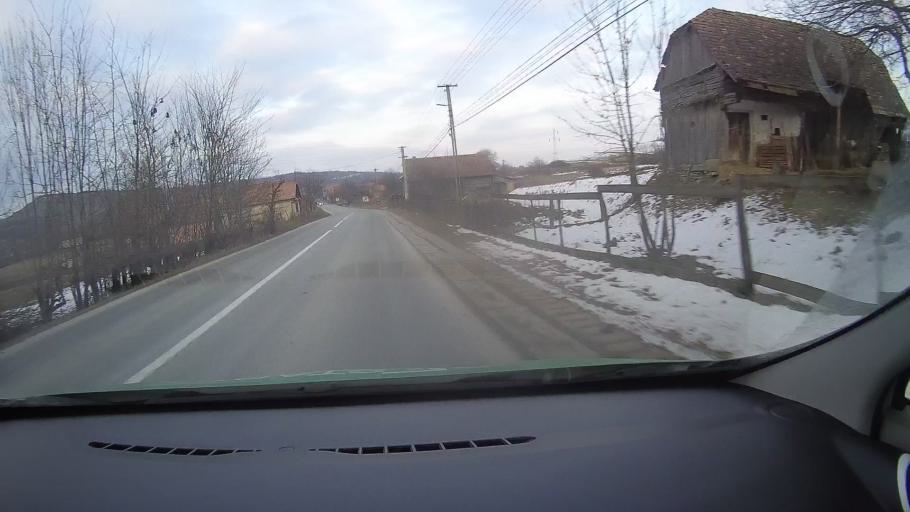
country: RO
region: Harghita
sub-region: Comuna Simonesti
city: Simonesti
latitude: 46.3542
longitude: 25.1349
